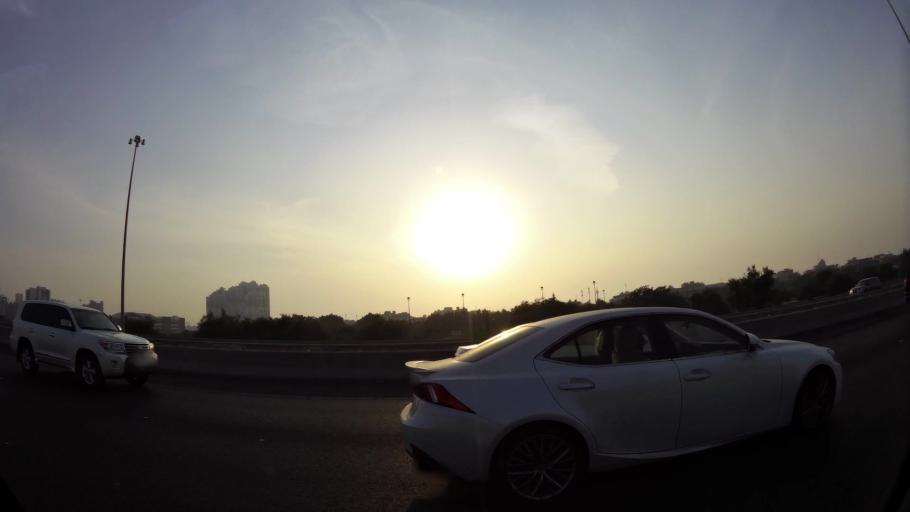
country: KW
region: Muhafazat Hawalli
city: Salwa
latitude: 29.2719
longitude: 48.0837
